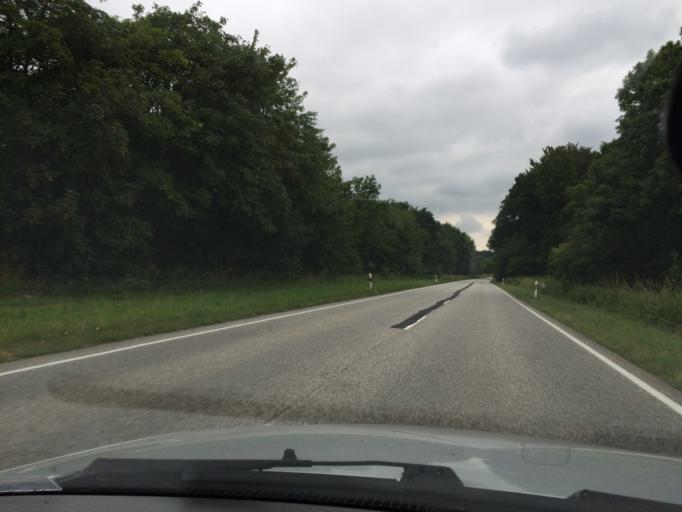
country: DE
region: Schleswig-Holstein
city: Oeversee
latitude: 54.6743
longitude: 9.4394
